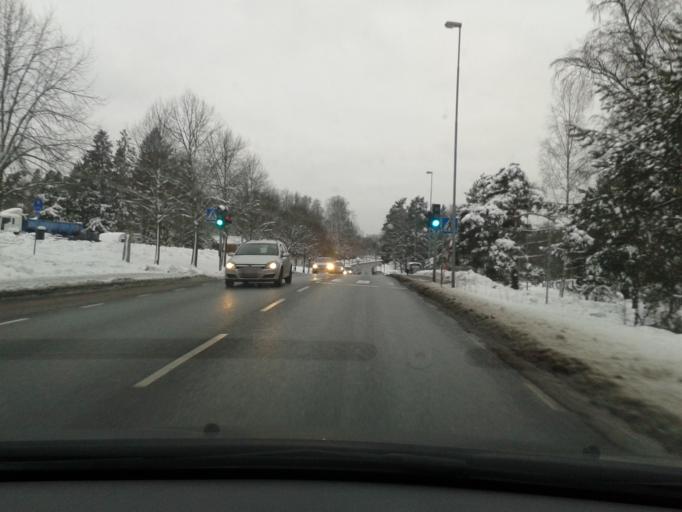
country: SE
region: Stockholm
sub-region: Nacka Kommun
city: Fisksatra
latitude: 59.2470
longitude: 18.2653
